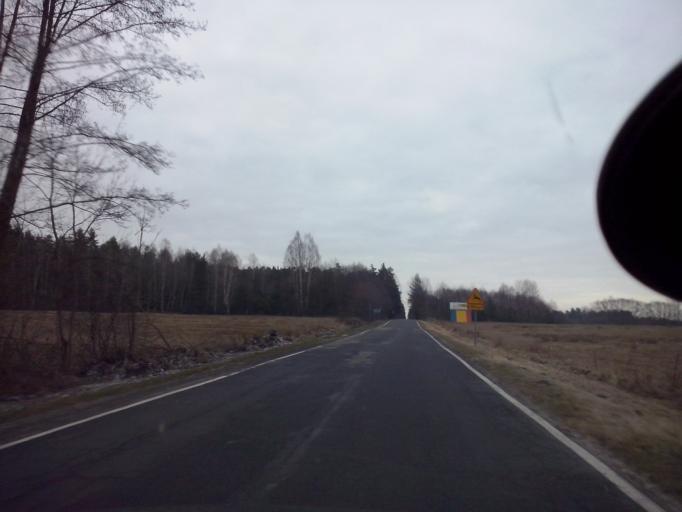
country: PL
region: Subcarpathian Voivodeship
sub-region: Powiat nizanski
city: Harasiuki
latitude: 50.4949
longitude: 22.5175
